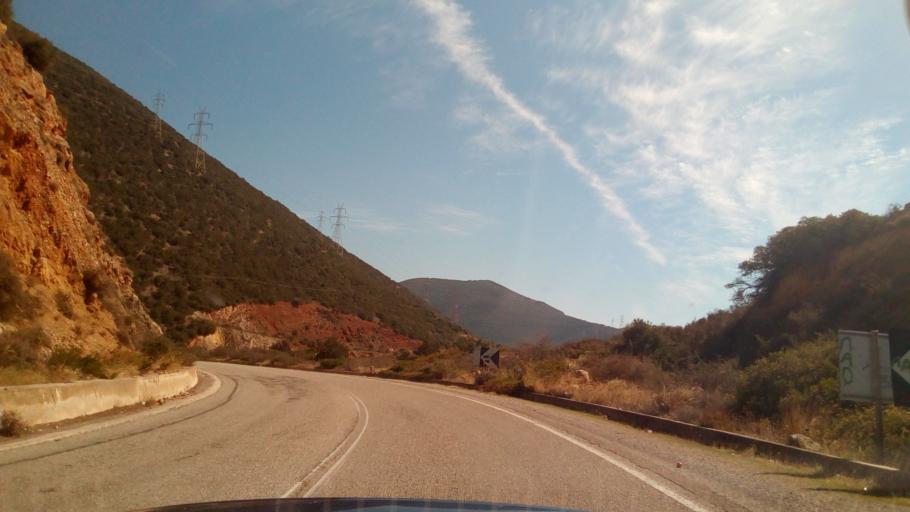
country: GR
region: West Greece
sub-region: Nomos Achaias
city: Selianitika
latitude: 38.3707
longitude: 22.1052
